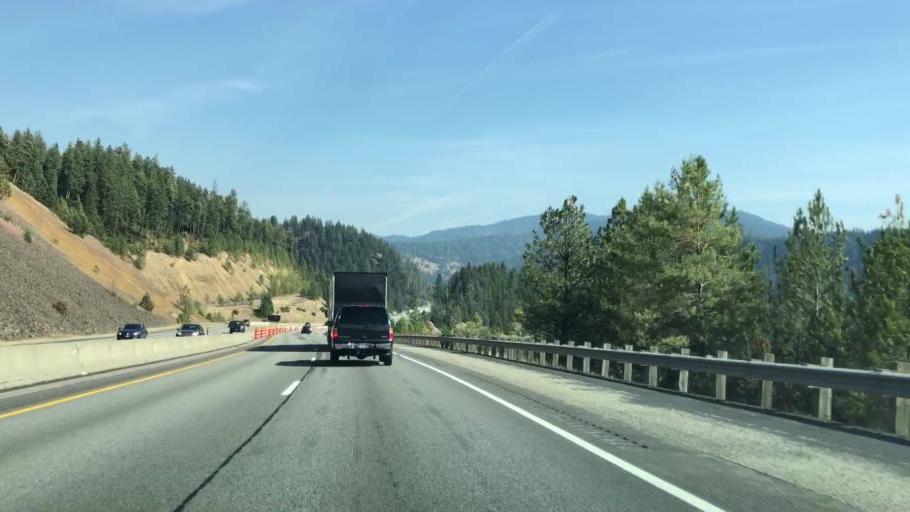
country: US
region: Idaho
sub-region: Kootenai County
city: Coeur d'Alene
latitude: 47.6307
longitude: -116.6897
